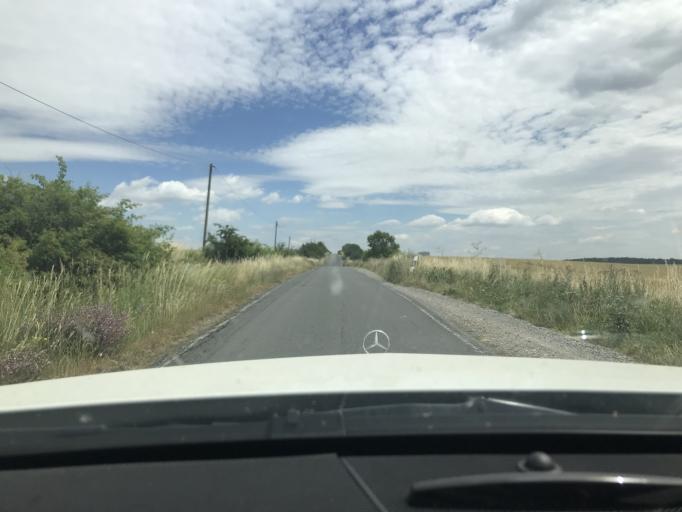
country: DE
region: Thuringia
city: Urbach
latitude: 51.2939
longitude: 10.6174
